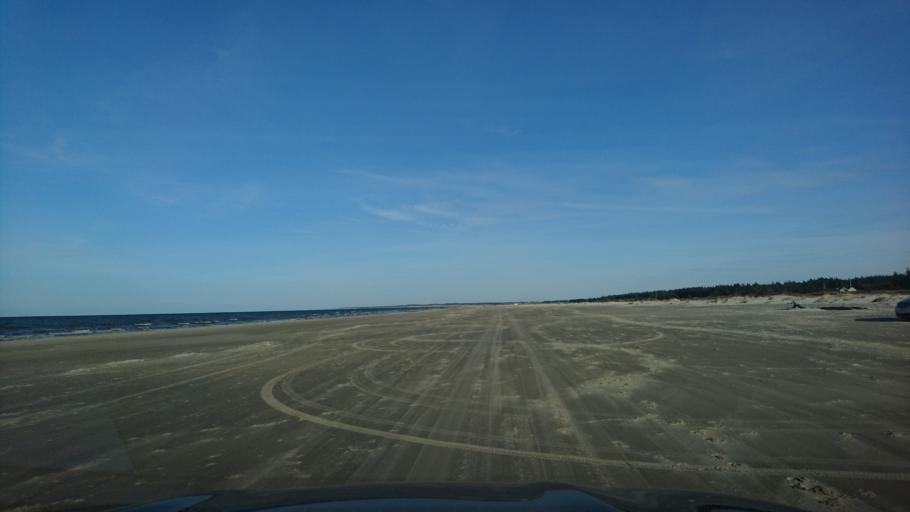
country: DK
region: North Denmark
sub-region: Hjorring Kommune
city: Hirtshals
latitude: 57.5896
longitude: 10.0946
